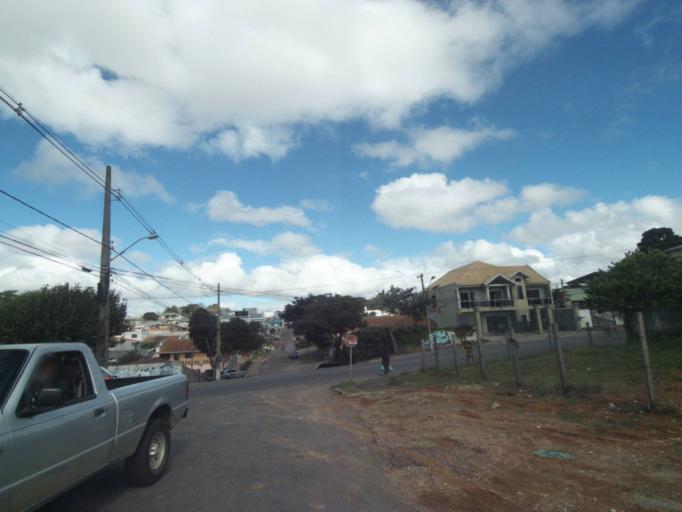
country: BR
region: Parana
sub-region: Sao Jose Dos Pinhais
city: Sao Jose dos Pinhais
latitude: -25.5405
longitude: -49.2923
